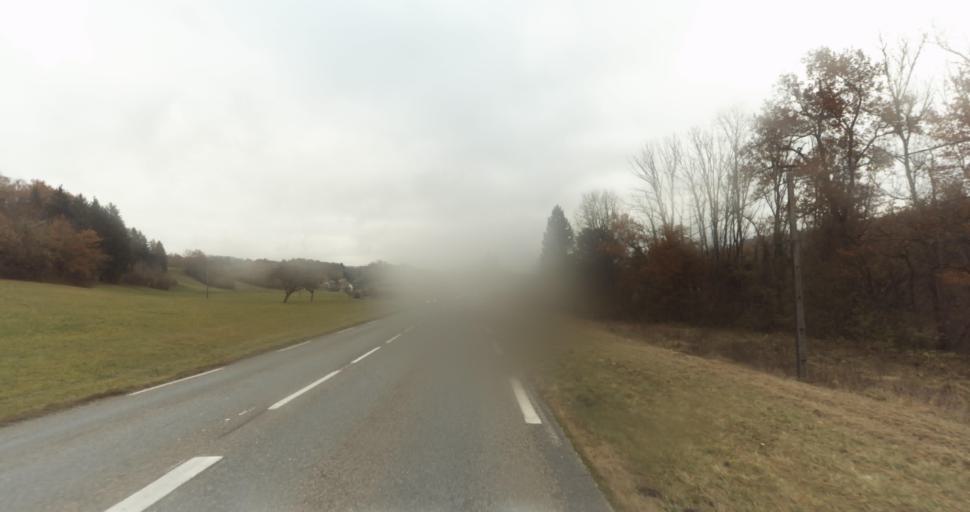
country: FR
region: Rhone-Alpes
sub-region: Departement de la Haute-Savoie
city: Groisy
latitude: 45.9968
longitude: 6.1761
